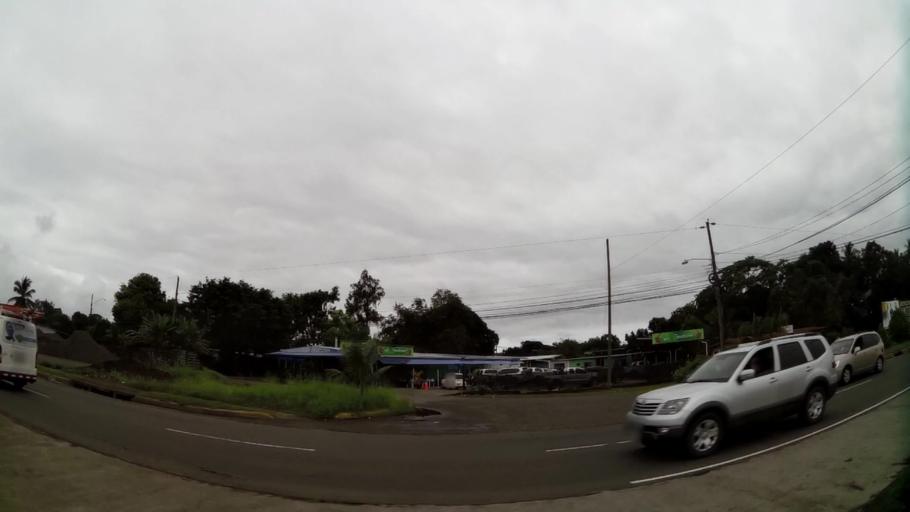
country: PA
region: Chiriqui
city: David
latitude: 8.4281
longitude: -82.4465
